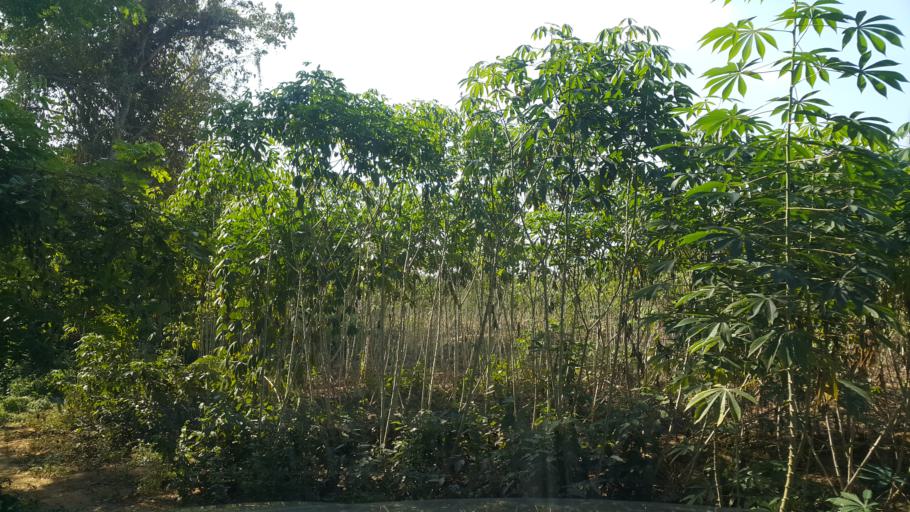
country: TH
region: Sukhothai
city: Thung Saliam
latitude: 17.3204
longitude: 99.5746
